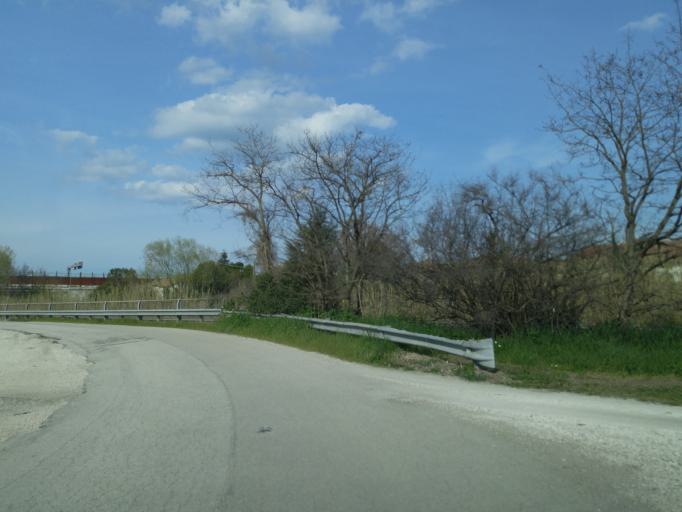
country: IT
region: The Marches
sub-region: Provincia di Pesaro e Urbino
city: Rosciano
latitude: 43.8126
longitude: 13.0176
